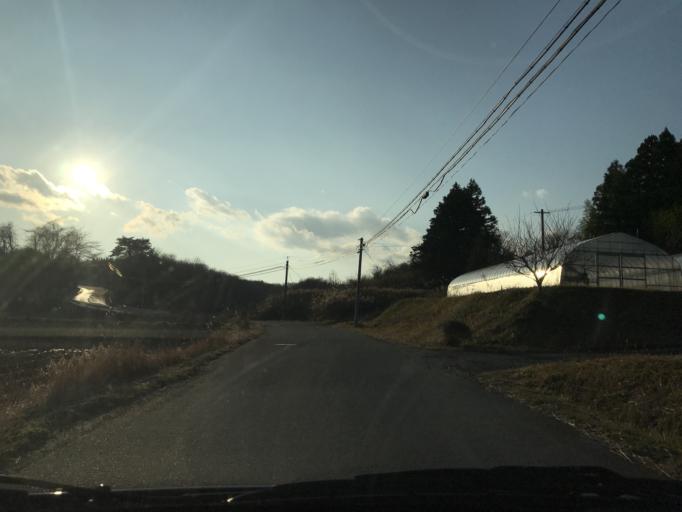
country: JP
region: Miyagi
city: Wakuya
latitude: 38.6971
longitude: 141.1091
